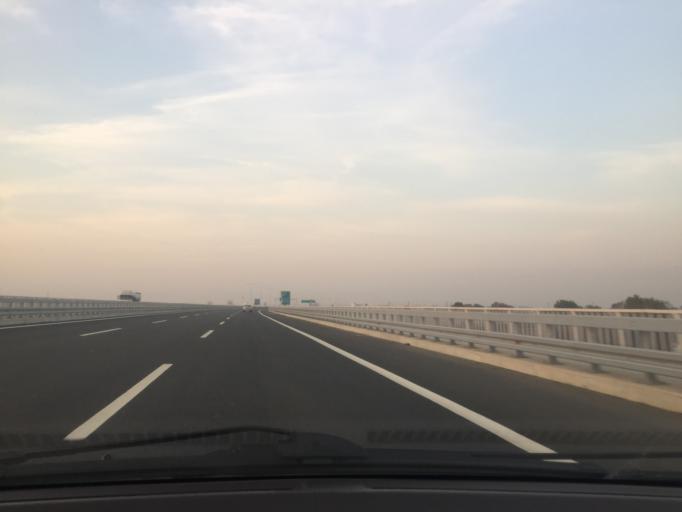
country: TR
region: Bursa
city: Karacabey
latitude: 40.2016
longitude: 28.3746
